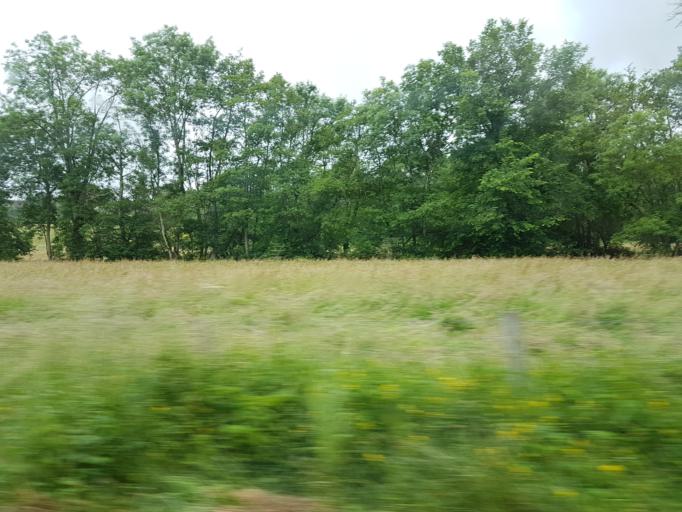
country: FR
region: Bourgogne
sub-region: Departement de la Nievre
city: Lormes
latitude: 47.1719
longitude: 3.8366
